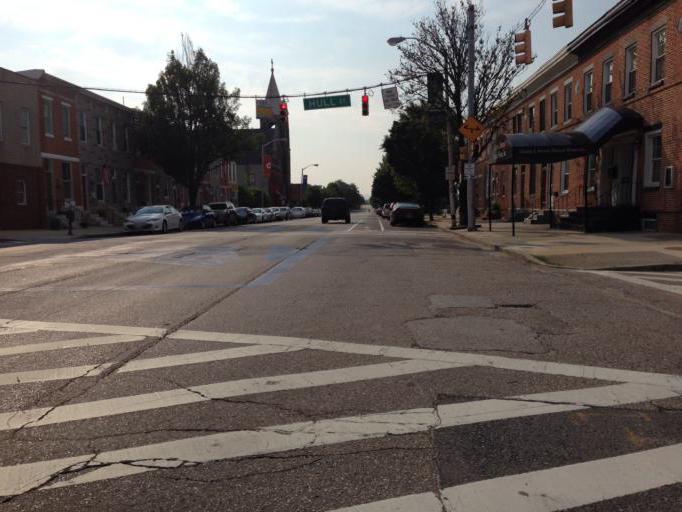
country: US
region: Maryland
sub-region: City of Baltimore
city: Baltimore
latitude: 39.2691
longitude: -76.5940
